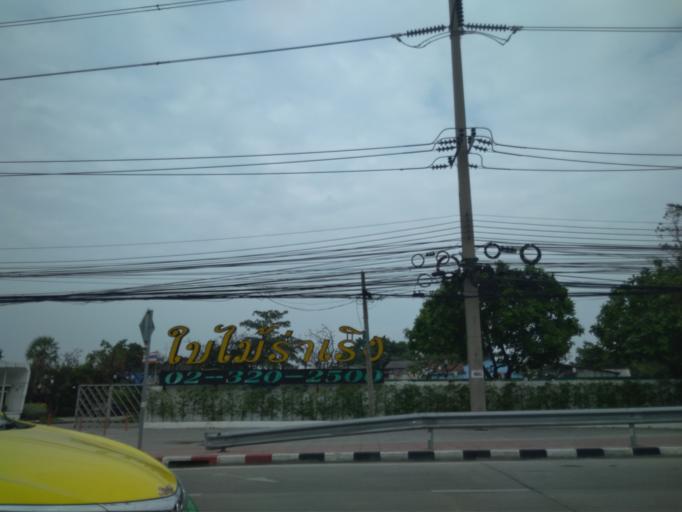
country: TH
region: Bangkok
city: Suan Luang
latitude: 13.7143
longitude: 100.6435
